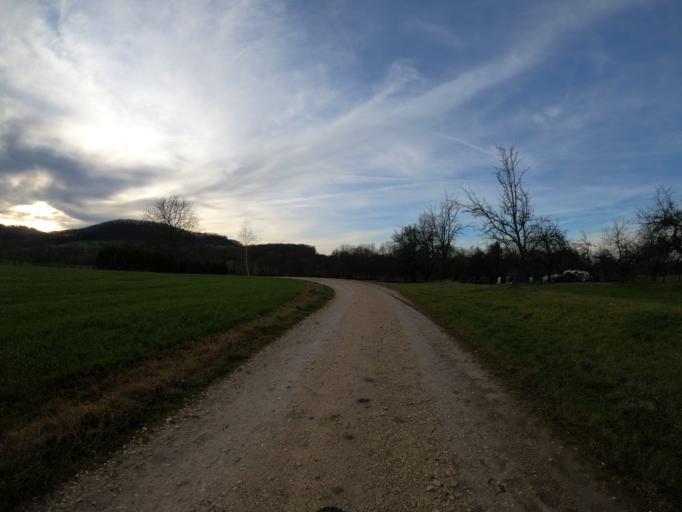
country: DE
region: Baden-Wuerttemberg
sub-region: Regierungsbezirk Stuttgart
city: Zell unter Aichelberg
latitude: 48.6393
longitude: 9.5904
